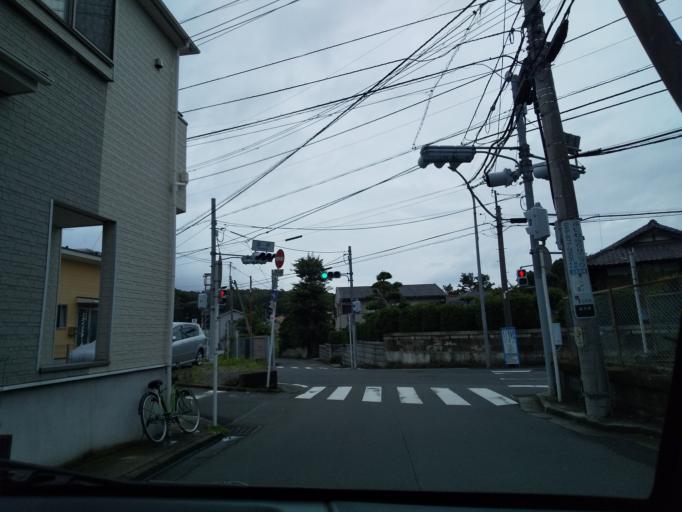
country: JP
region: Kanagawa
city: Fujisawa
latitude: 35.3919
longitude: 139.5098
